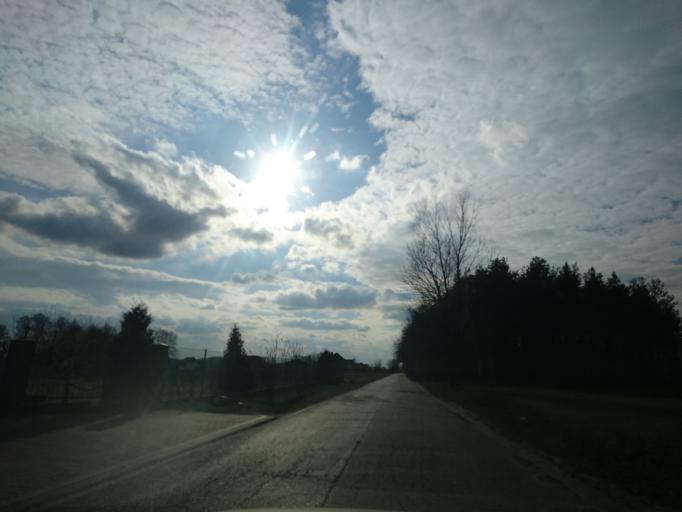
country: PL
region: Kujawsko-Pomorskie
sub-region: Powiat torunski
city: Lubicz Gorny
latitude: 53.0388
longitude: 18.8008
